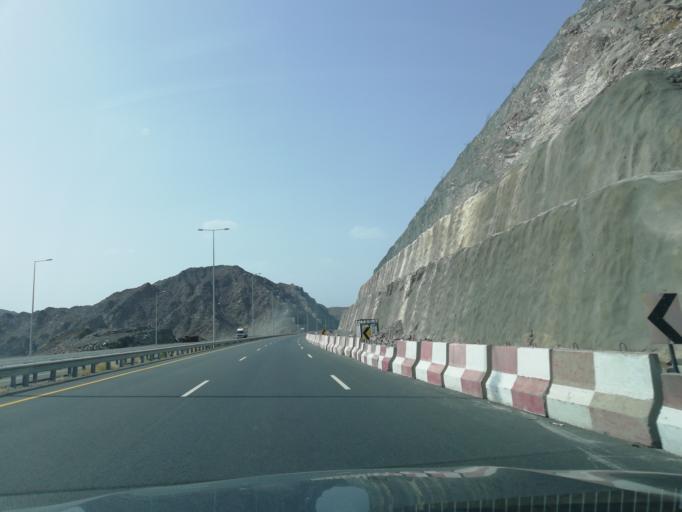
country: OM
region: Muhafazat ad Dakhiliyah
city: Sufalat Sama'il
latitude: 22.9816
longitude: 58.2328
